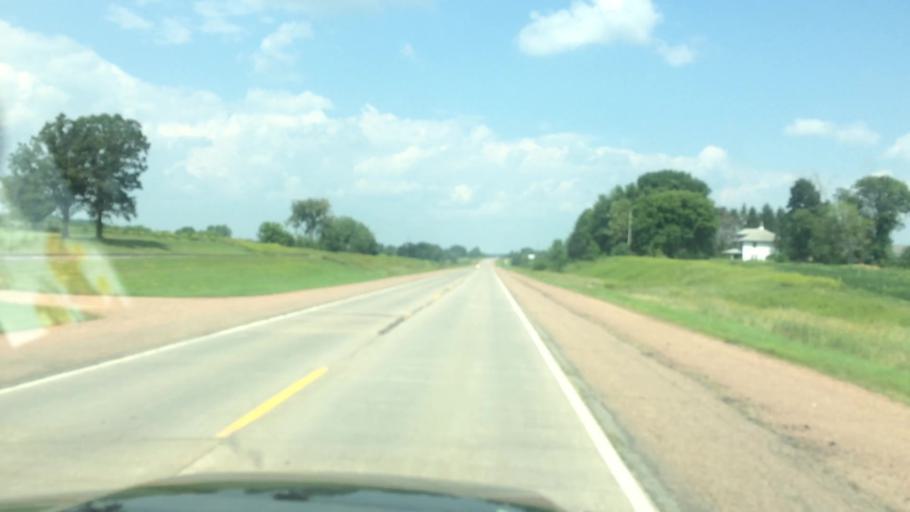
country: US
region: Wisconsin
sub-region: Clark County
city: Colby
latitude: 44.8684
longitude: -90.3158
